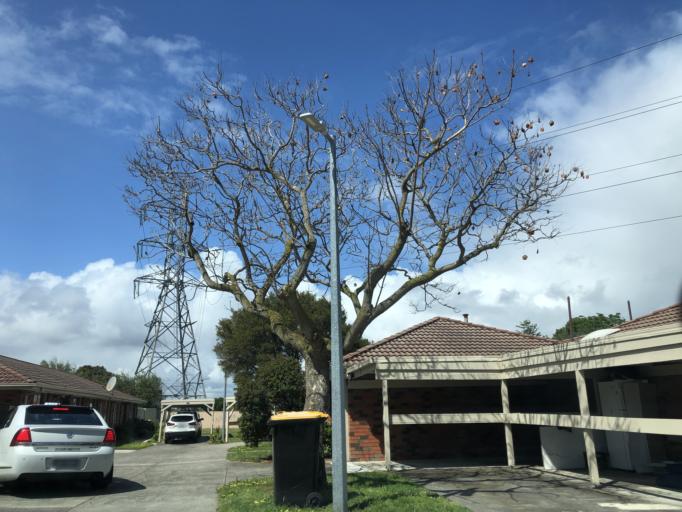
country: AU
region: Victoria
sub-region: Kingston
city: Clayton South
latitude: -37.9369
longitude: 145.1046
